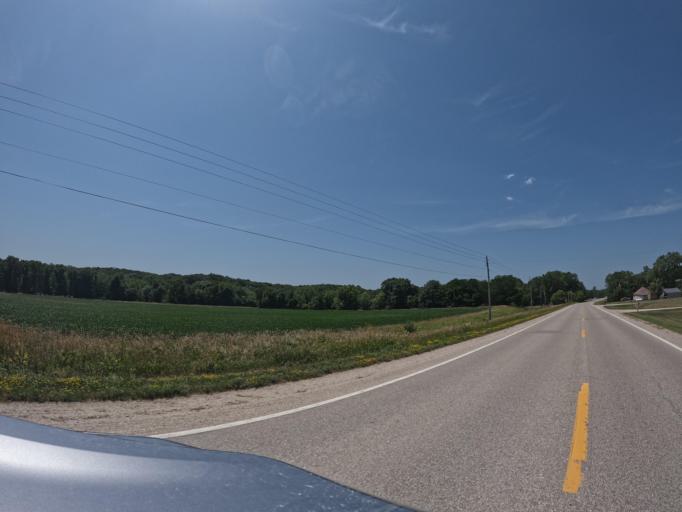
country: US
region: Iowa
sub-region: Henry County
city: Mount Pleasant
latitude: 40.9374
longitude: -91.6104
